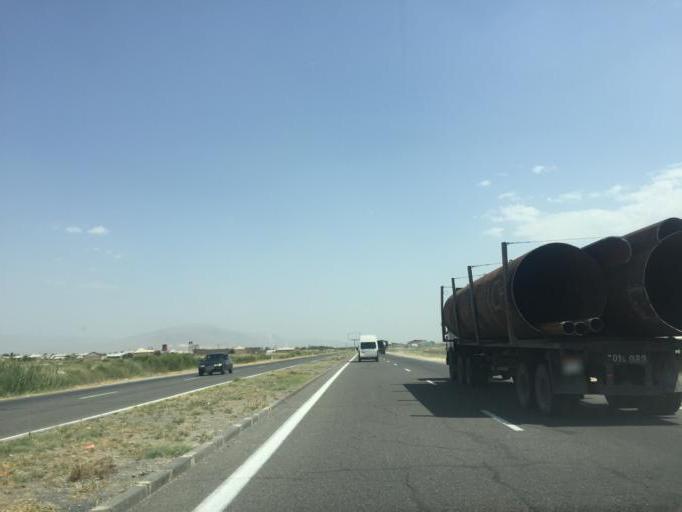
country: AM
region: Ararat
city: Shahumyan
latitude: 39.9256
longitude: 44.5779
